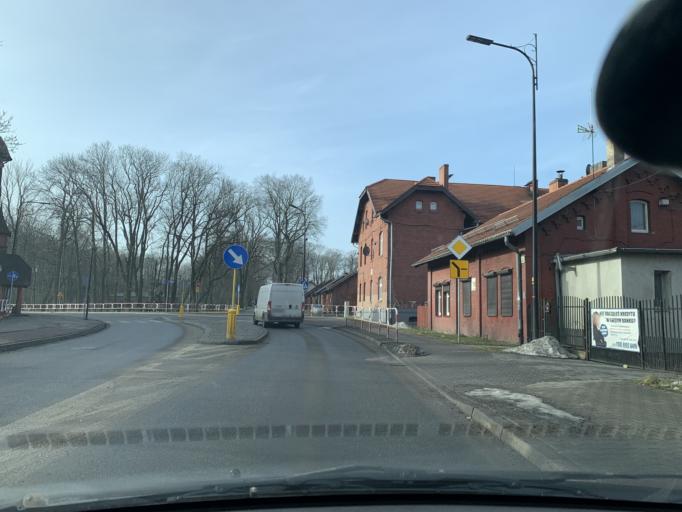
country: PL
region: Silesian Voivodeship
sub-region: Ruda Slaska
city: Ruda Slaska
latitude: 50.3186
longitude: 18.8562
